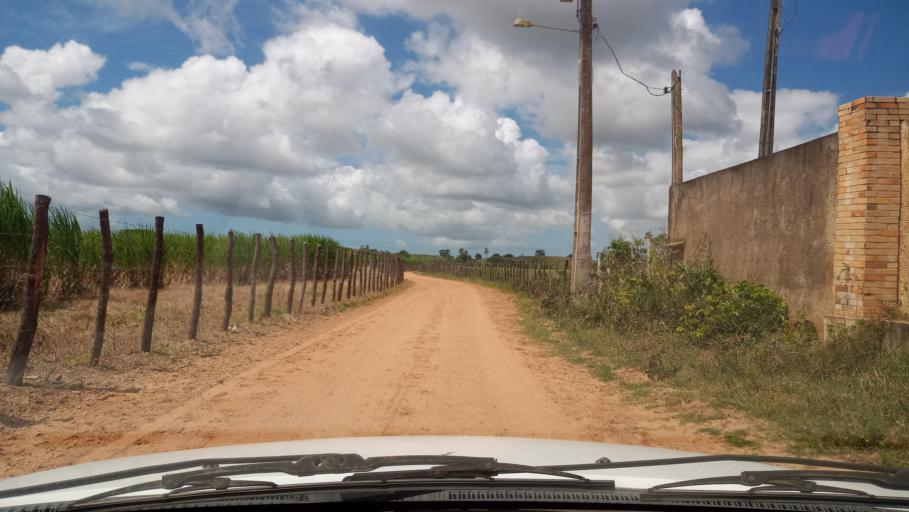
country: BR
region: Rio Grande do Norte
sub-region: Goianinha
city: Goianinha
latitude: -6.2606
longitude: -35.2446
